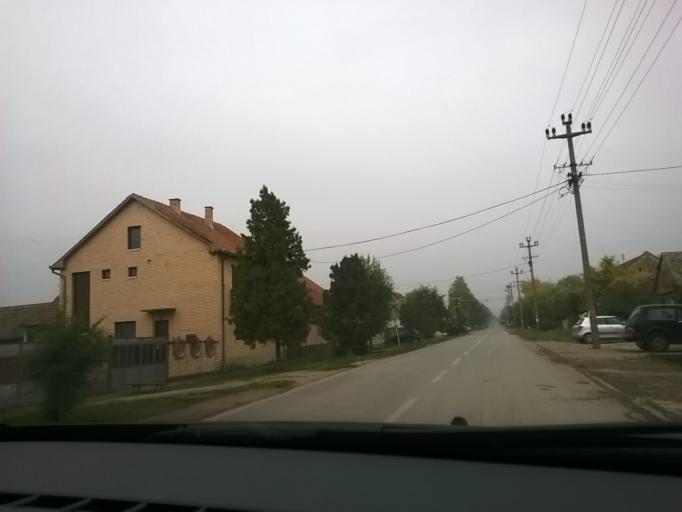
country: RS
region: Autonomna Pokrajina Vojvodina
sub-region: Juznobanatski Okrug
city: Kovin
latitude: 44.8799
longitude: 20.9711
